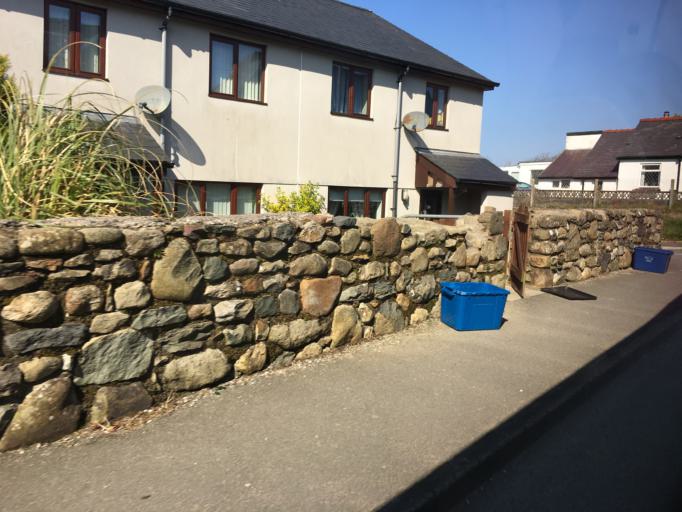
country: GB
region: Wales
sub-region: Gwynedd
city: Llanwnda
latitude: 53.0450
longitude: -4.2815
